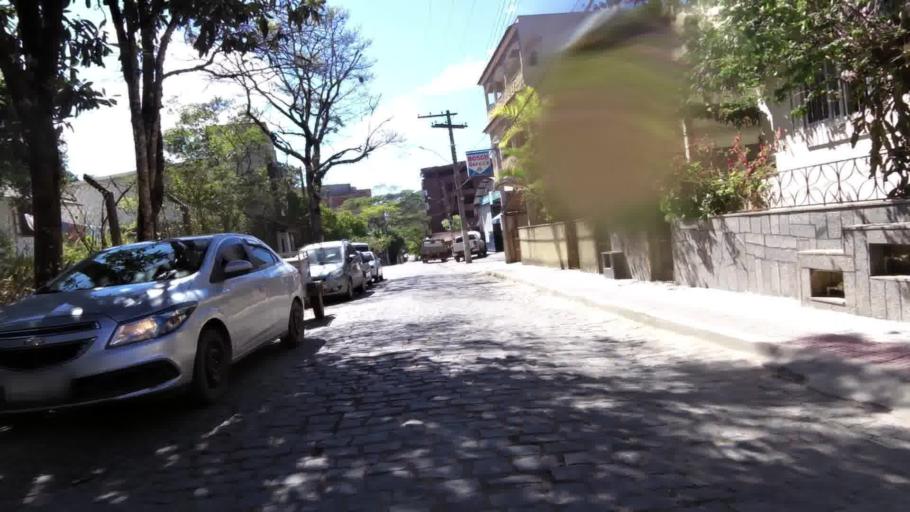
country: BR
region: Espirito Santo
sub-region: Vargem Alta
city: Vargem Alta
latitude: -20.6741
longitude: -41.0134
